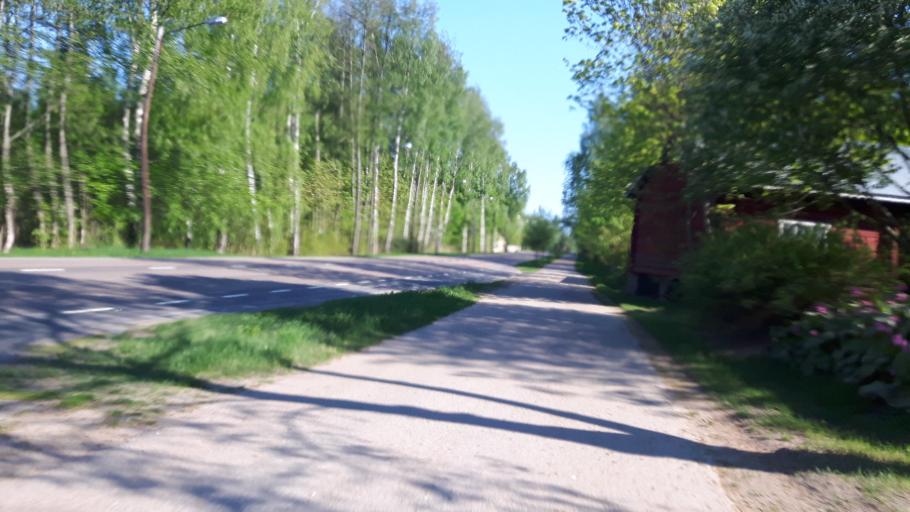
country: FI
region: Kymenlaakso
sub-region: Kotka-Hamina
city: Kotka
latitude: 60.4552
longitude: 26.8912
